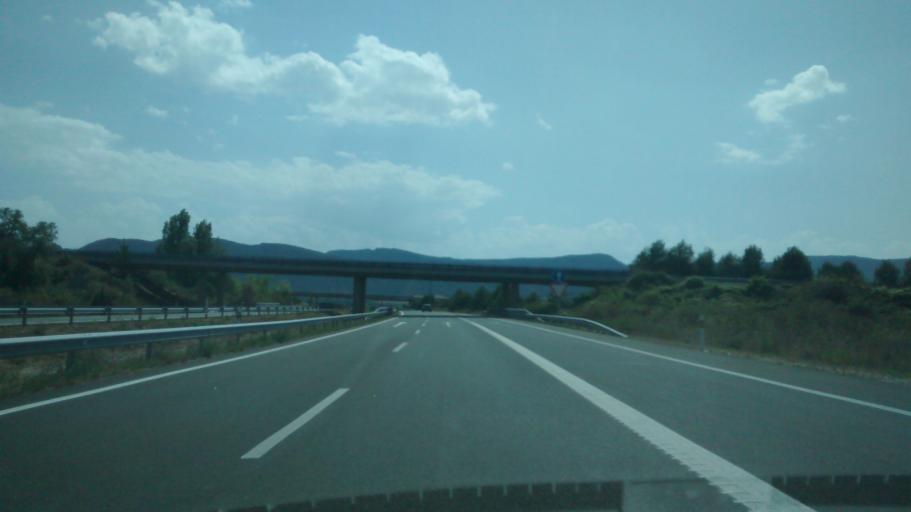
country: ES
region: Basque Country
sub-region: Provincia de Alava
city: Zambrana
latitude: 42.6761
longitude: -2.8900
